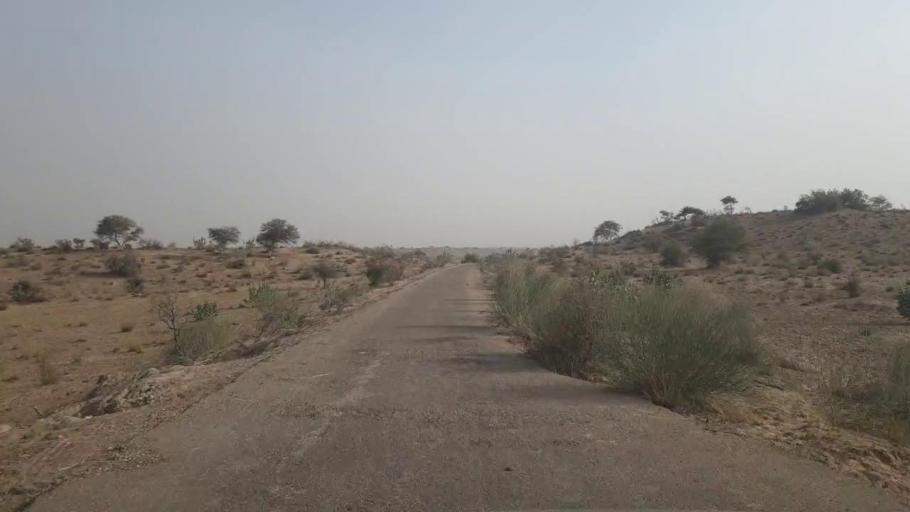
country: PK
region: Sindh
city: Chor
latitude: 25.5075
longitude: 69.9688
